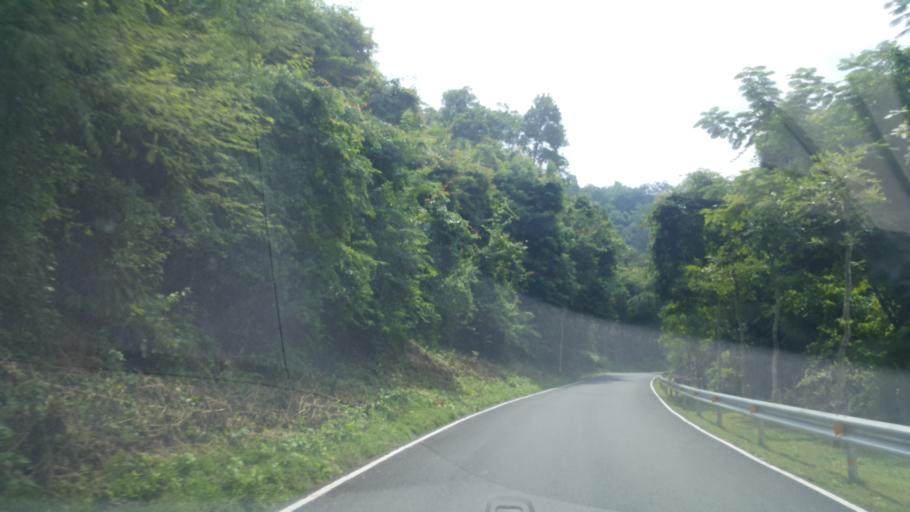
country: TH
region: Chon Buri
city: Ban Bueng
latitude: 13.2102
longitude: 101.0595
